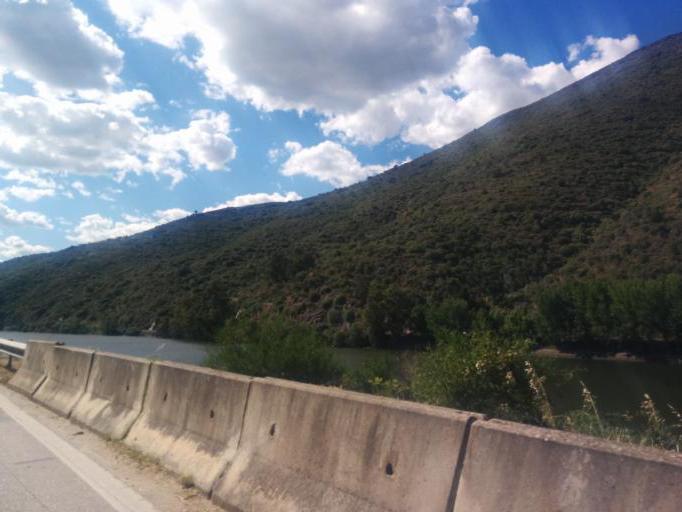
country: PT
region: Viseu
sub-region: Armamar
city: Armamar
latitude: 41.1426
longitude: -7.7064
